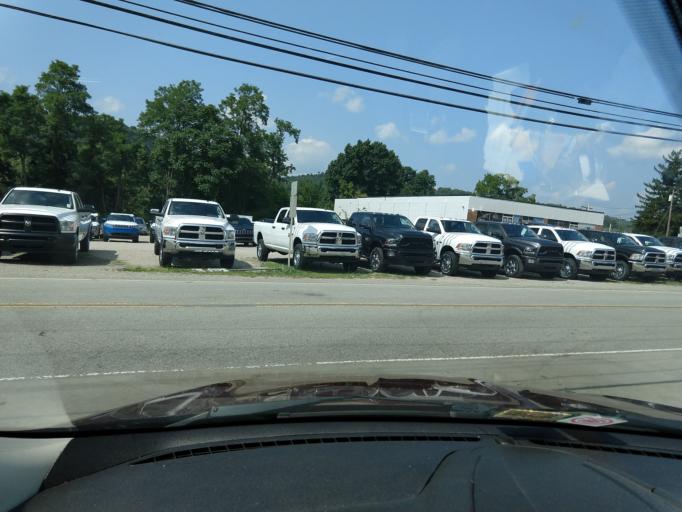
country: US
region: Pennsylvania
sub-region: Greene County
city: Morrisville
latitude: 39.8968
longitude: -80.1621
